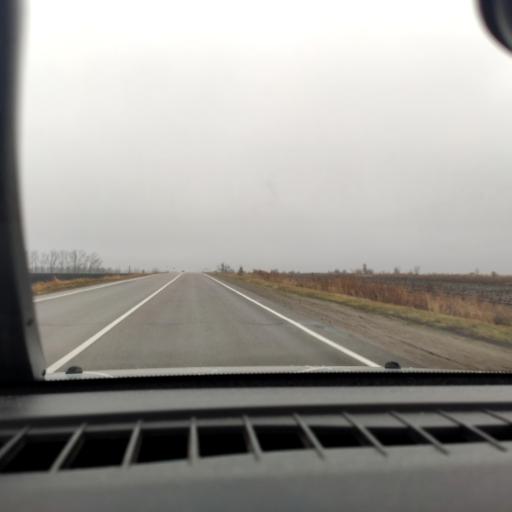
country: RU
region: Voronezj
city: Shilovo
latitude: 51.4603
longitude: 38.9702
